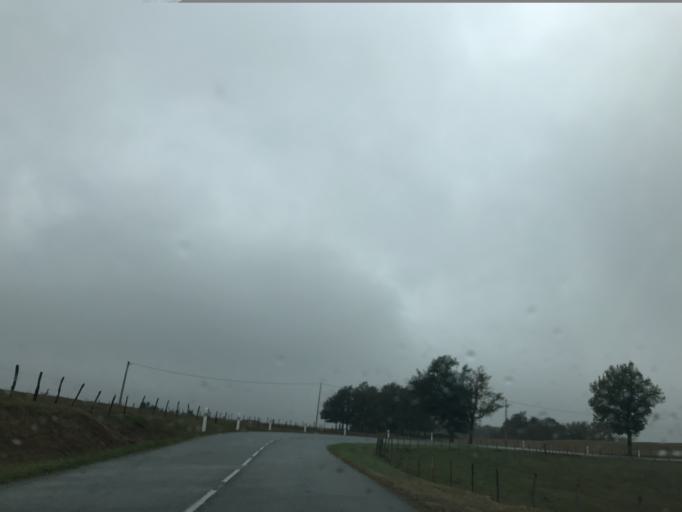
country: FR
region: Auvergne
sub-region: Departement du Puy-de-Dome
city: Courpiere
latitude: 45.7682
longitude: 3.5158
